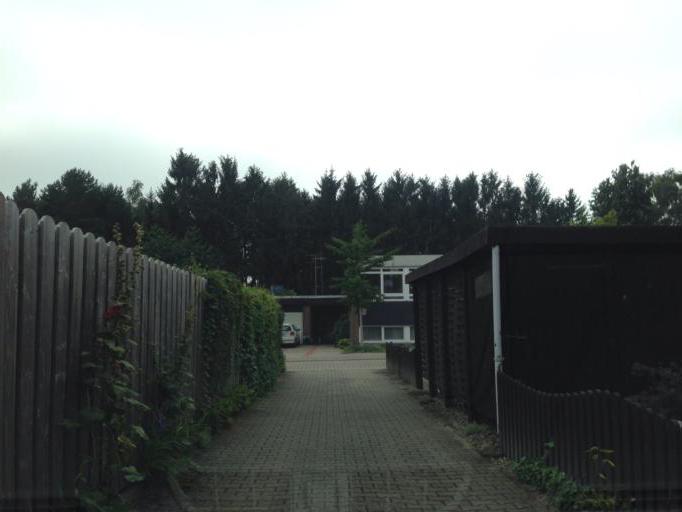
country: DE
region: Lower Saxony
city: Adendorf
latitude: 53.2829
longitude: 10.4311
